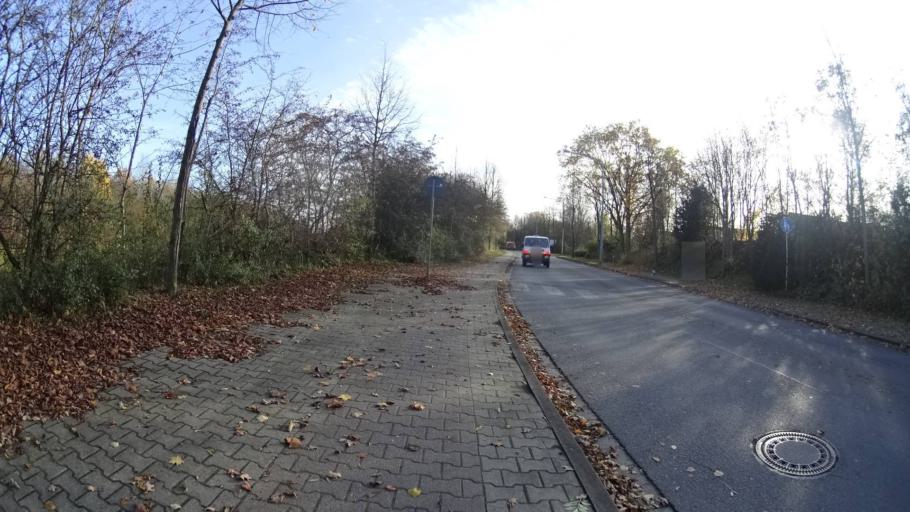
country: DE
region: Lower Saxony
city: Lueneburg
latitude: 53.2503
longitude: 10.4453
